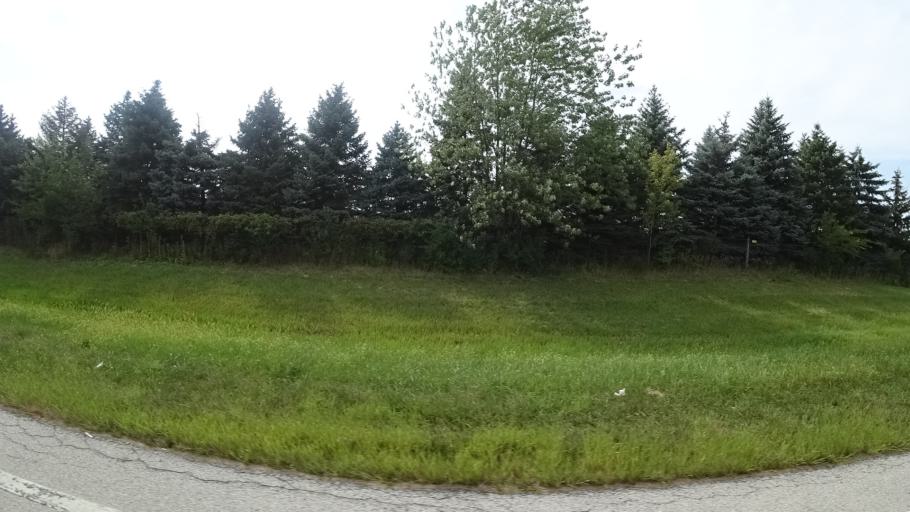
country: US
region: Illinois
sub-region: Will County
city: Frankfort Square
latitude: 41.5308
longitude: -87.7710
